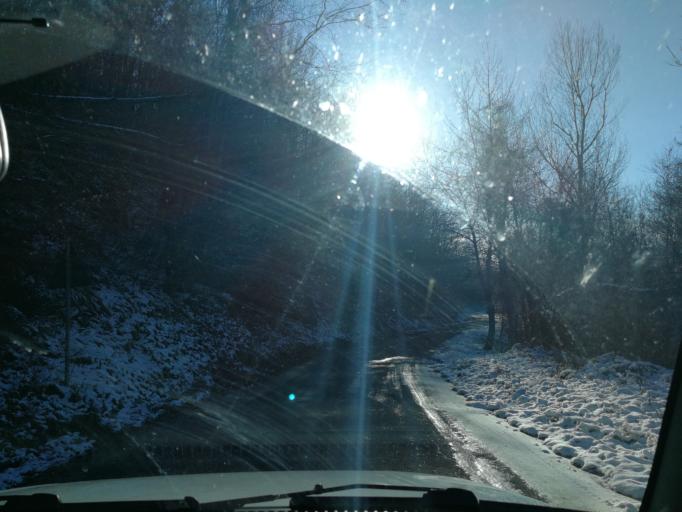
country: IT
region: Latium
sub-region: Provincia di Rieti
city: Amatrice
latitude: 42.6688
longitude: 13.2916
